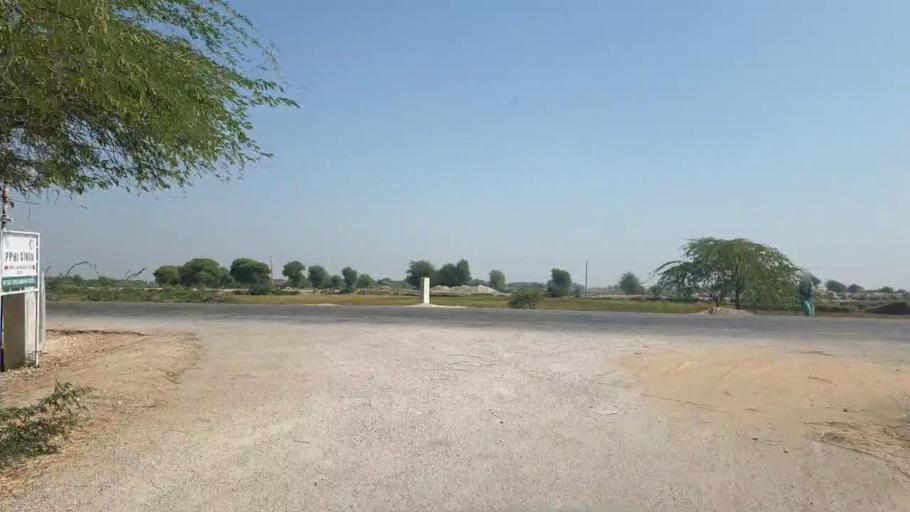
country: PK
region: Sindh
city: Talhar
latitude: 24.7985
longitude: 68.8152
